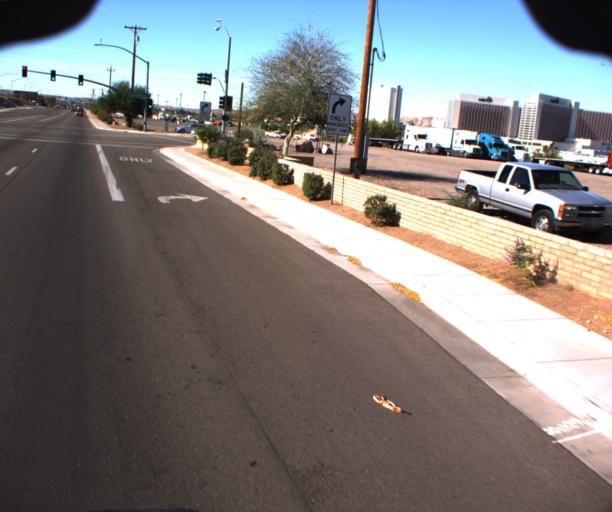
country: US
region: Nevada
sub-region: Clark County
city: Laughlin
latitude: 35.1688
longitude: -114.5662
